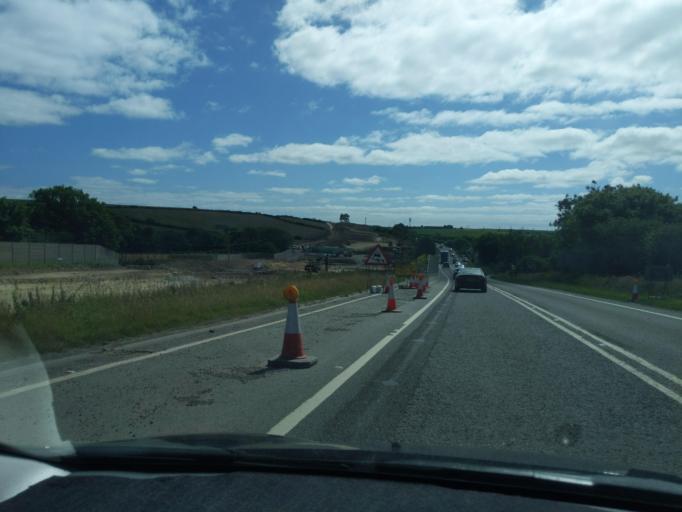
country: GB
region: England
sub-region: Cornwall
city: Truro
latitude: 50.3122
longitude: -5.0894
